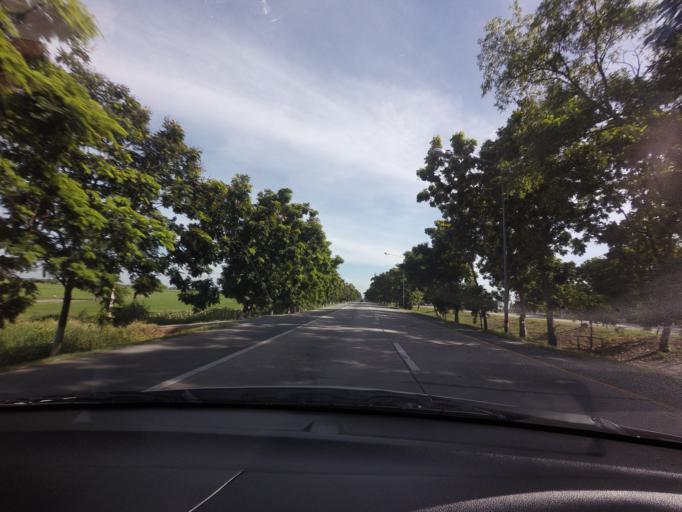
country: TH
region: Suphan Buri
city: Bang Pla Ma
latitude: 14.3681
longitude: 100.1817
